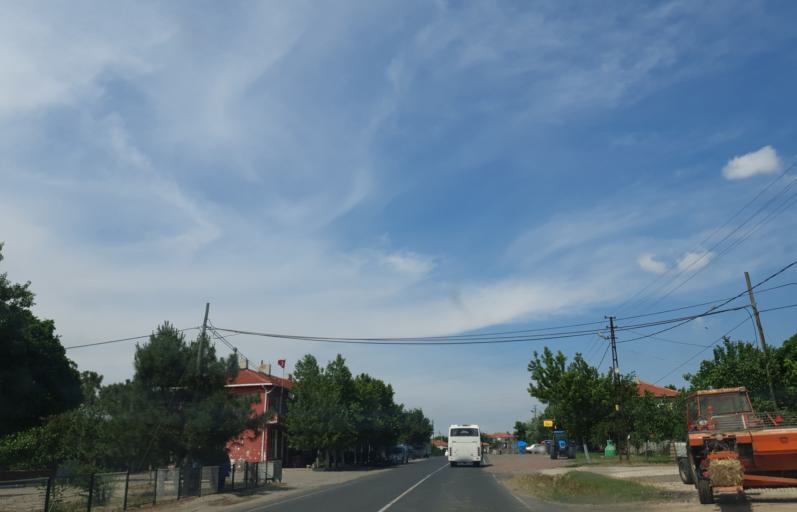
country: TR
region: Kirklareli
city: Buyukkaristiran
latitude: 41.2314
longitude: 27.5819
